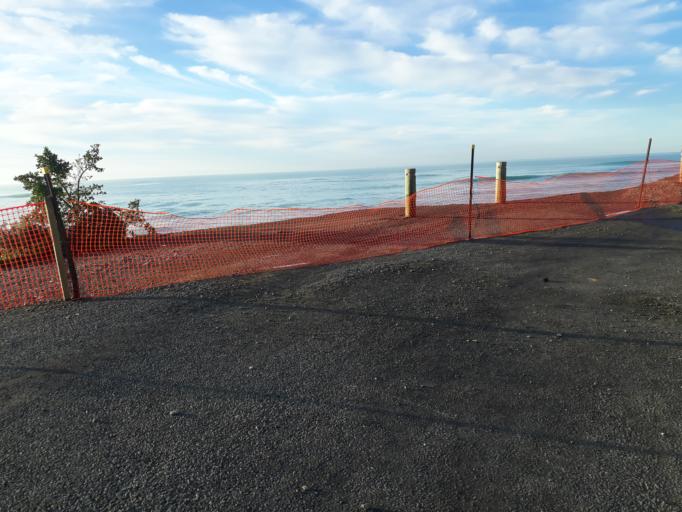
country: NZ
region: Canterbury
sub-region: Timaru District
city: Timaru
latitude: -44.4129
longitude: 171.2647
